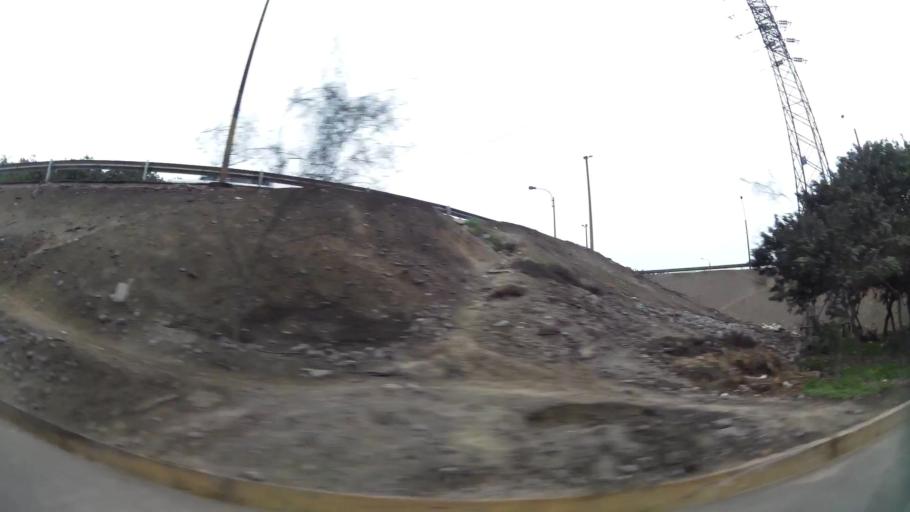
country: PE
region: Lima
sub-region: Lima
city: San Luis
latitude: -12.0863
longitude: -76.9842
